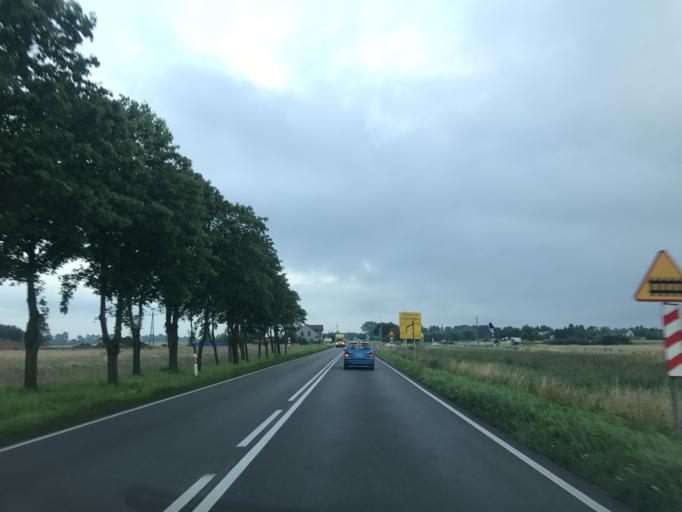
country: PL
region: West Pomeranian Voivodeship
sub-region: Powiat goleniowski
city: Nowogard
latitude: 53.7273
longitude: 15.1987
